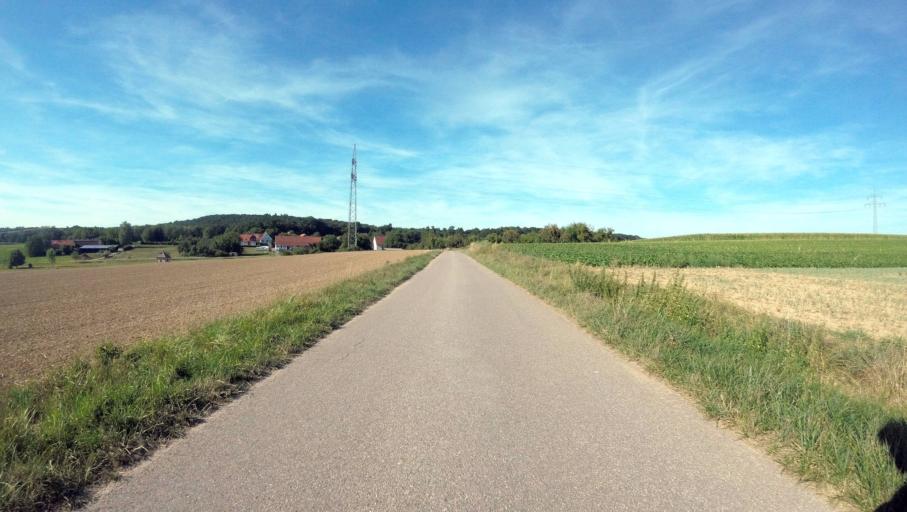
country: DE
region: Baden-Wuerttemberg
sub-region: Regierungsbezirk Stuttgart
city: Kirchberg an der Murr
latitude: 48.9612
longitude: 9.3542
